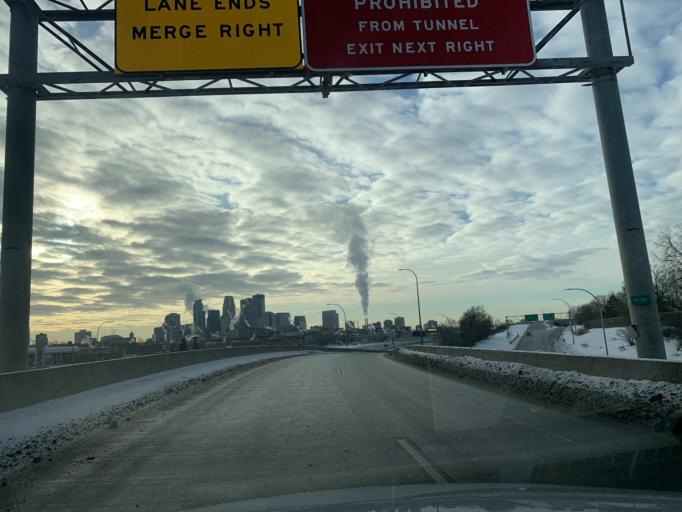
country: US
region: Minnesota
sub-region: Hennepin County
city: Minneapolis
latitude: 44.9981
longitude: -93.2836
